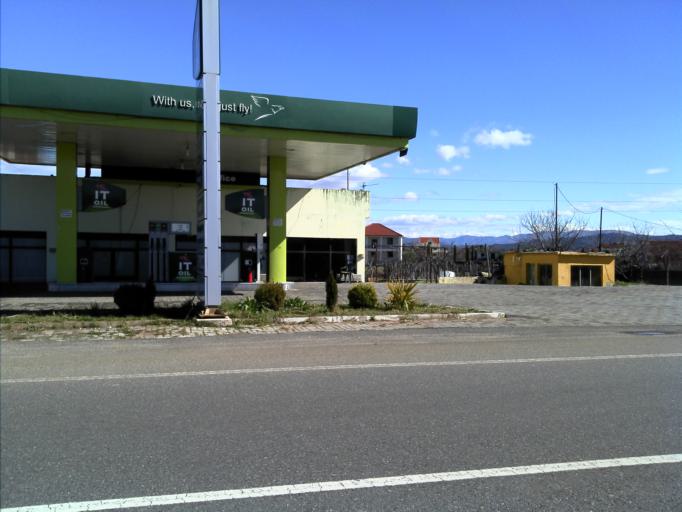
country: AL
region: Shkoder
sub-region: Rrethi i Shkodres
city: Shkoder
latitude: 42.0998
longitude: 19.5053
